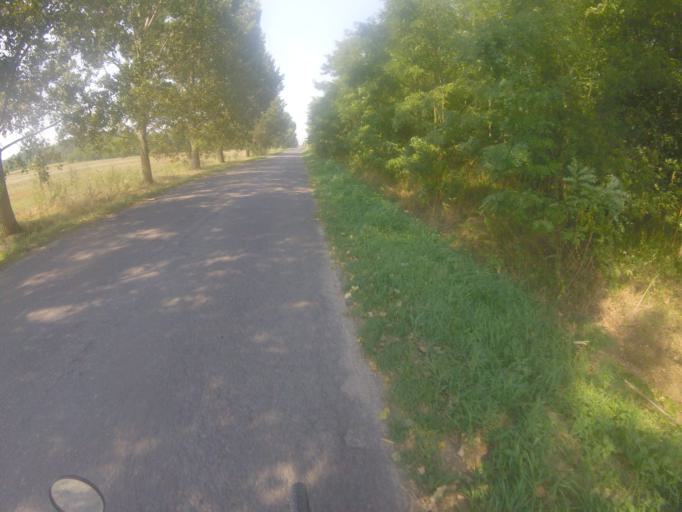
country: HU
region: Bacs-Kiskun
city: Ersekcsanad
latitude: 46.2539
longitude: 18.9659
